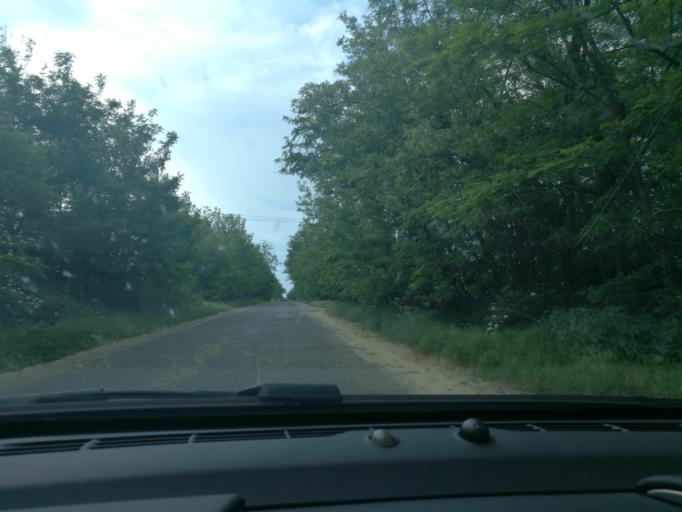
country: HU
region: Szabolcs-Szatmar-Bereg
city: Nyirpazony
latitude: 47.9333
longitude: 21.7963
